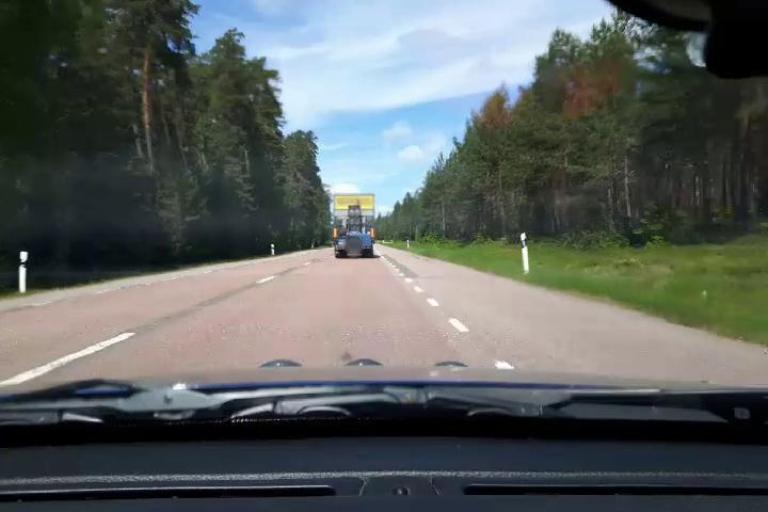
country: SE
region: Uppsala
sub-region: Osthammars Kommun
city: Bjorklinge
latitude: 60.1263
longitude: 17.5093
